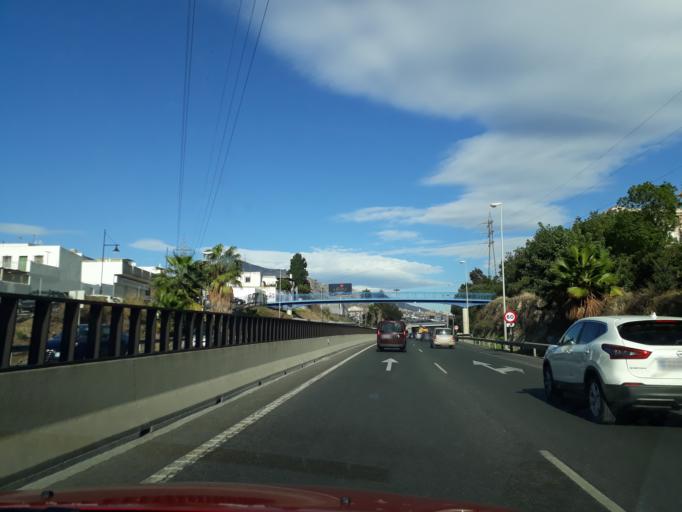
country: ES
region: Andalusia
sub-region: Provincia de Malaga
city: Fuengirola
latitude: 36.5488
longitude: -4.6302
